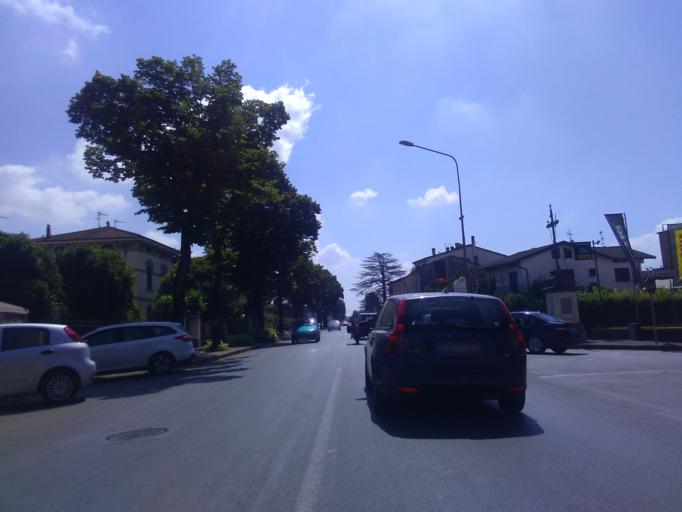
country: IT
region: Tuscany
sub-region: Provincia di Lucca
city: Lucca
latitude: 43.8481
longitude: 10.4686
